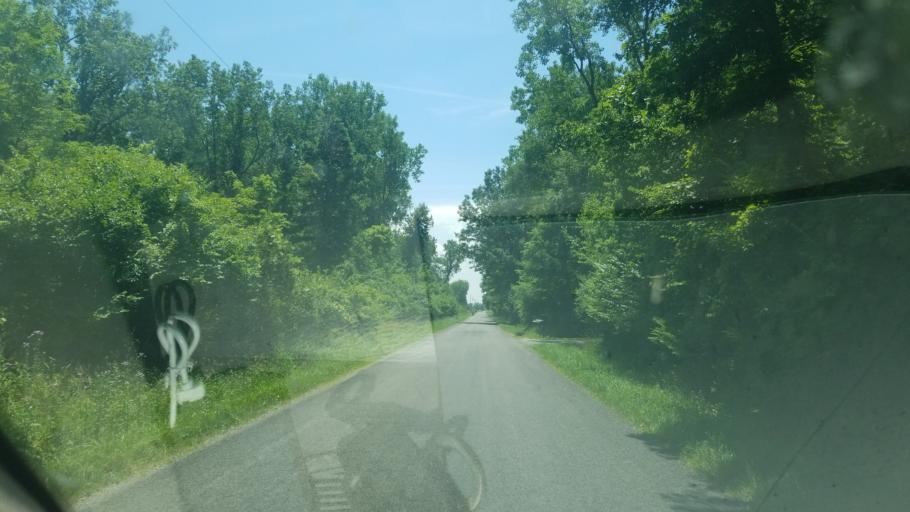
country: US
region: Ohio
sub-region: Hancock County
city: Findlay
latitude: 41.0033
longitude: -83.6363
